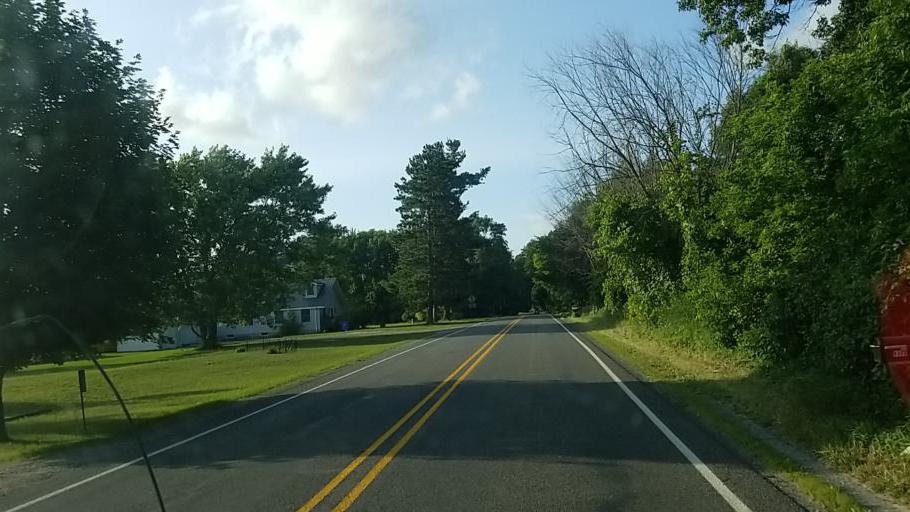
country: US
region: Michigan
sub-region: Montcalm County
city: Greenville
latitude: 43.2073
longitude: -85.3518
